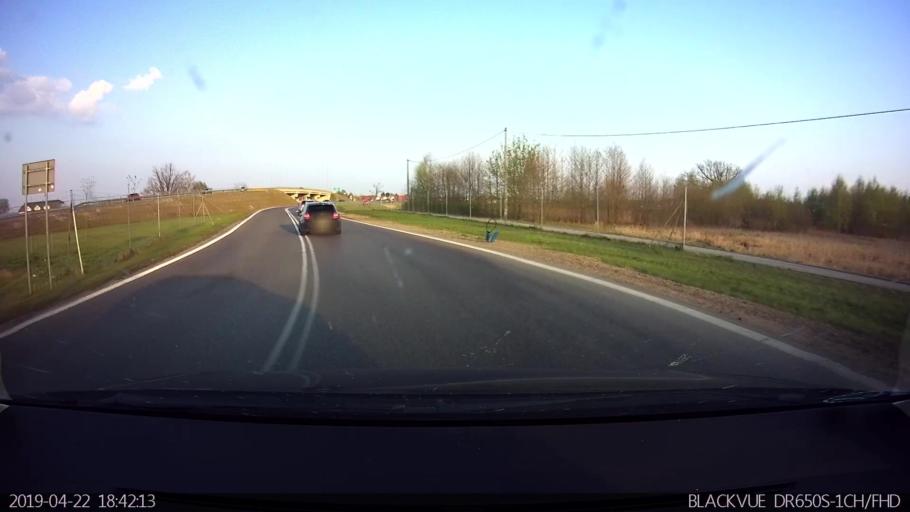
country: PL
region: Masovian Voivodeship
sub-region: Powiat wolominski
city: Dabrowka
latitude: 52.4488
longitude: 21.2599
